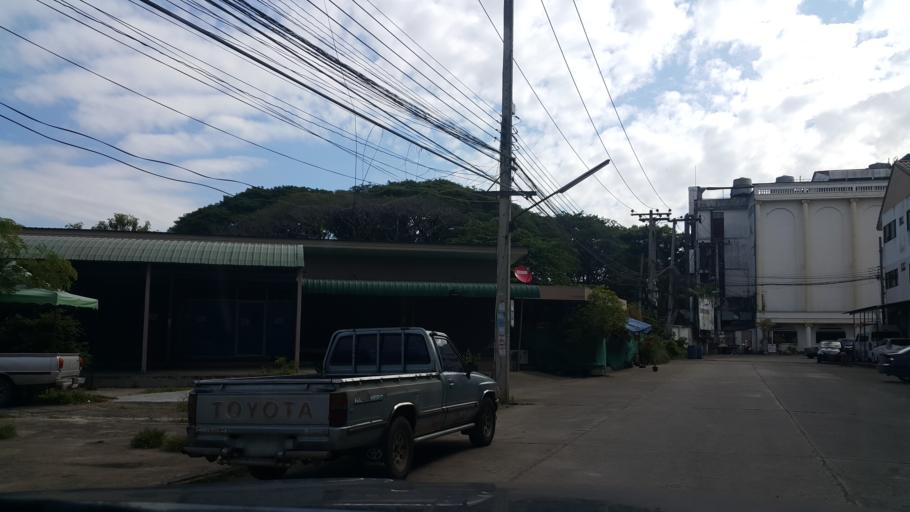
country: TH
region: Chiang Mai
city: Chiang Mai
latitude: 18.7885
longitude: 99.0141
